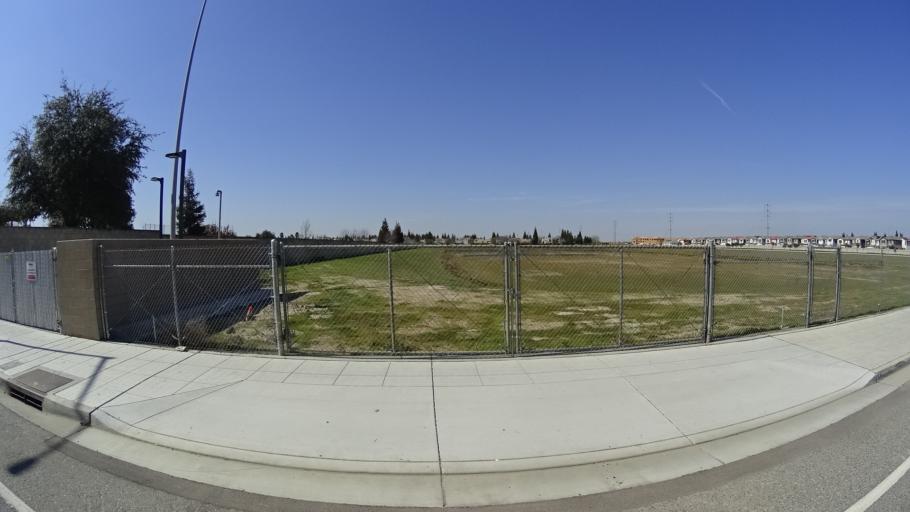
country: US
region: California
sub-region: Fresno County
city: Clovis
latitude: 36.8943
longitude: -119.7568
